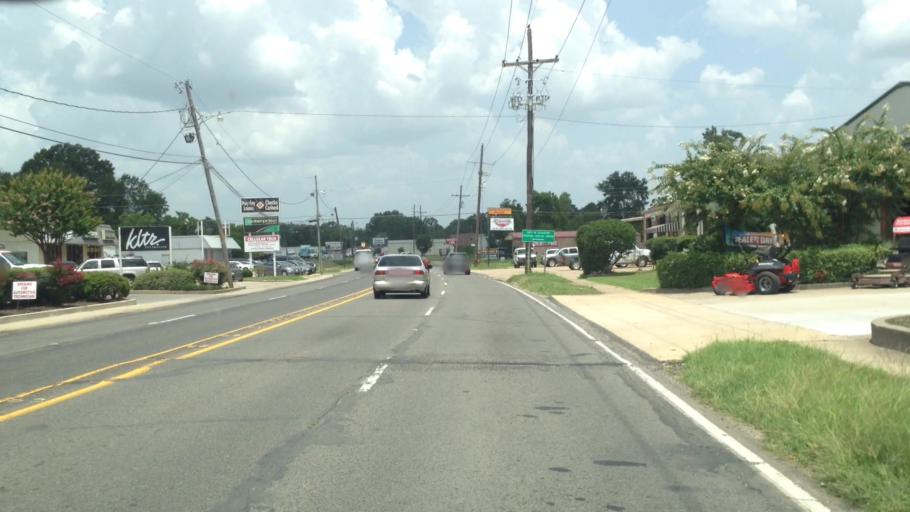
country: US
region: Louisiana
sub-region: Ouachita Parish
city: West Monroe
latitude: 32.5151
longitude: -92.1379
